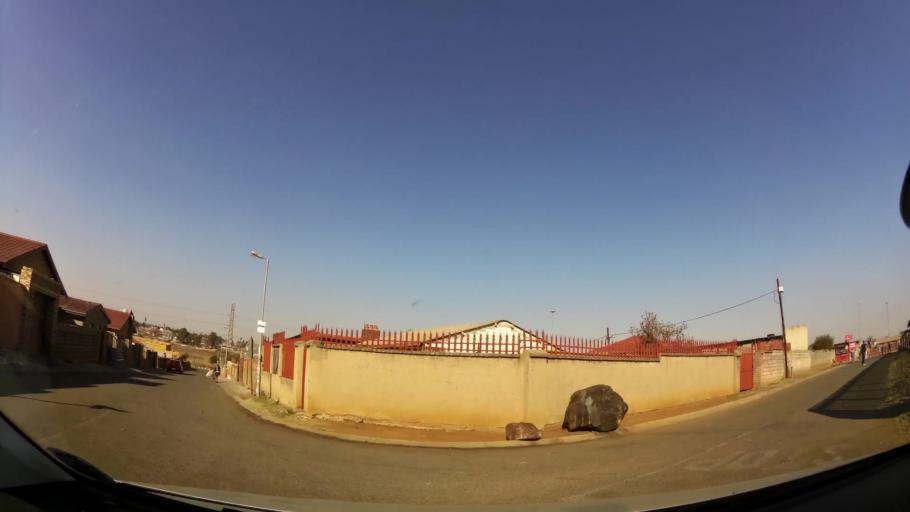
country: ZA
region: Gauteng
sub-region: City of Johannesburg Metropolitan Municipality
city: Soweto
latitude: -26.2720
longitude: 27.8800
